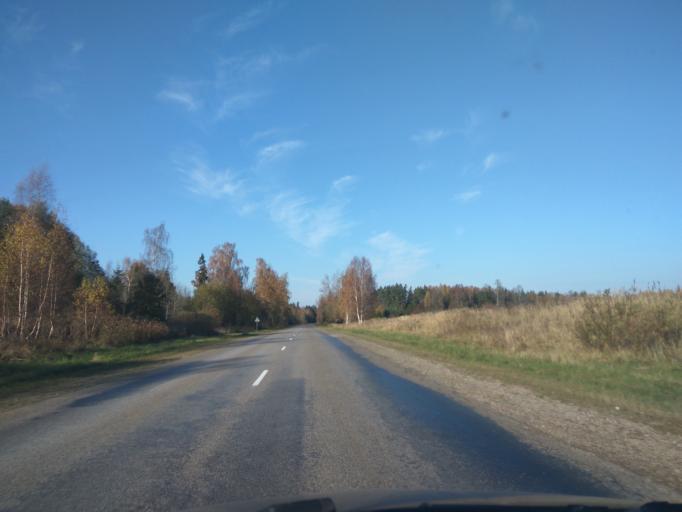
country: LV
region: Kuldigas Rajons
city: Kuldiga
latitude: 57.0408
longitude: 21.8309
